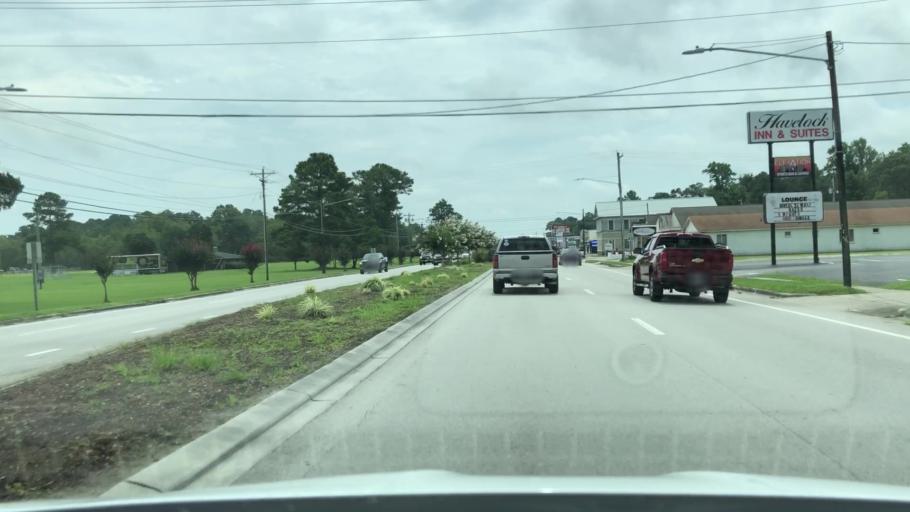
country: US
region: North Carolina
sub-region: Craven County
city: Havelock
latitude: 34.8749
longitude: -76.9032
